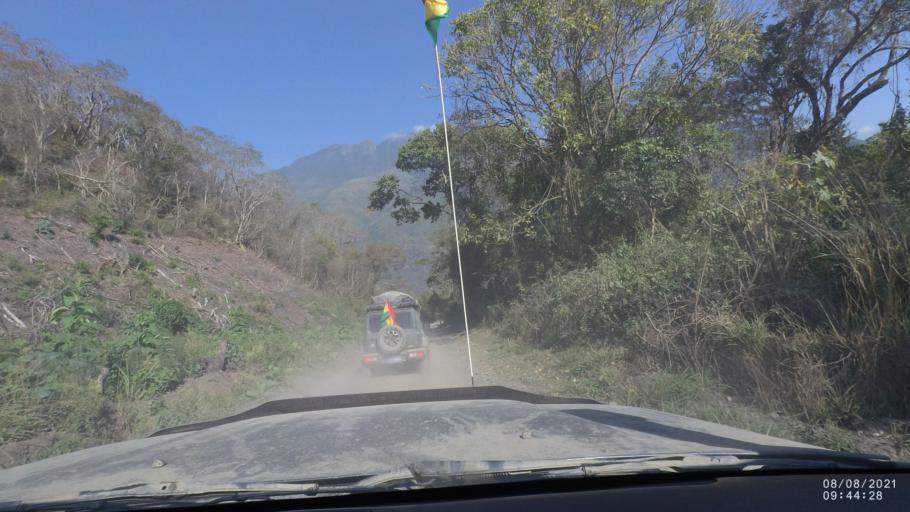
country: BO
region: La Paz
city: Quime
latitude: -16.6016
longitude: -66.7236
